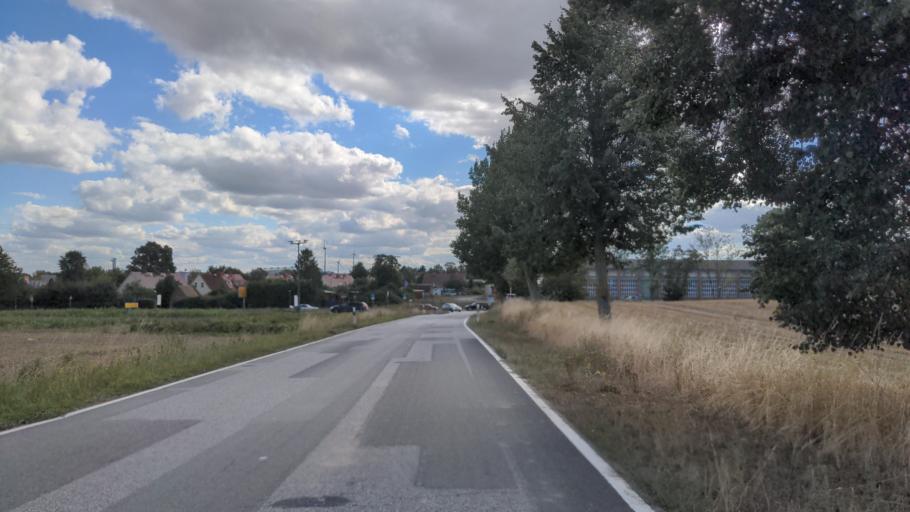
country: DE
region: Mecklenburg-Vorpommern
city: Gramkow
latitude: 53.9058
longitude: 11.3775
